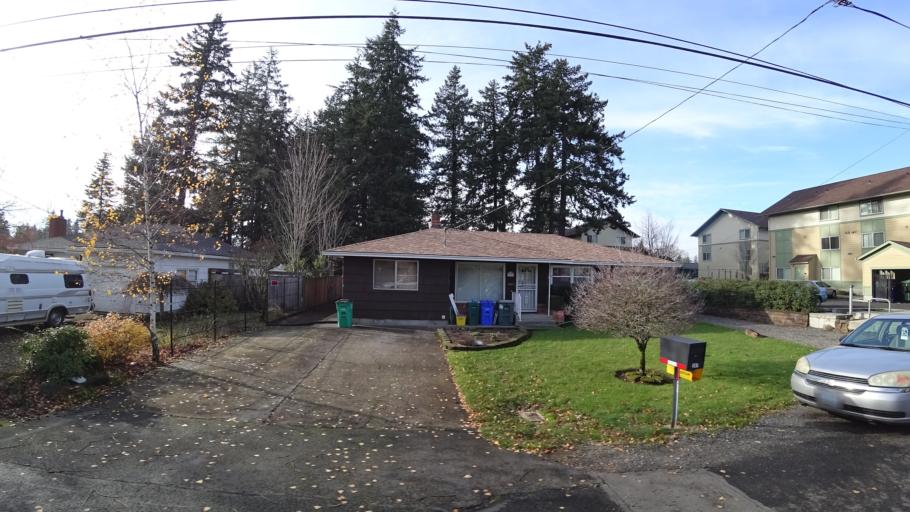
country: US
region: Oregon
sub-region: Multnomah County
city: Lents
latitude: 45.5216
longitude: -122.5184
